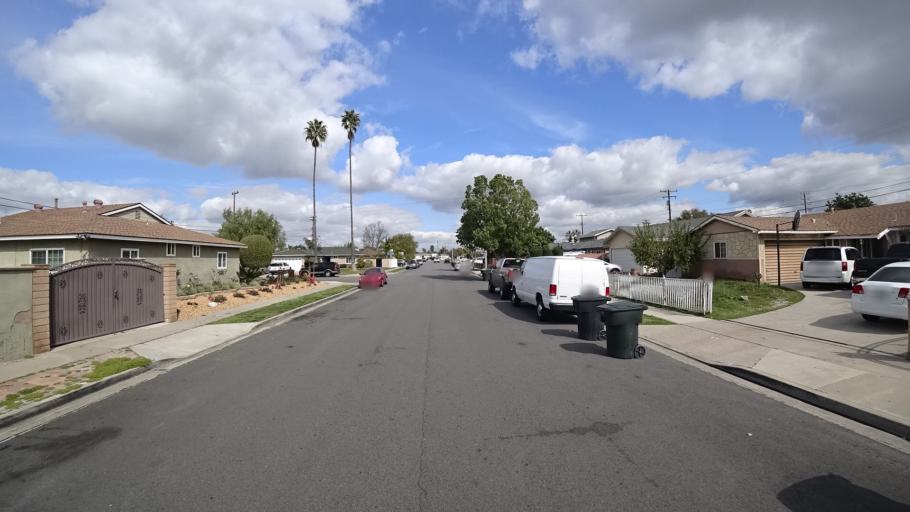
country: US
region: California
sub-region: Orange County
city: Buena Park
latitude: 33.8420
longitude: -117.9686
